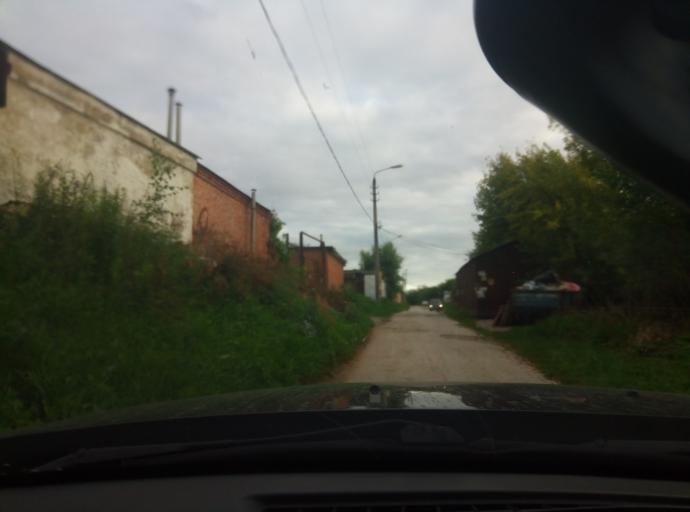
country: RU
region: Tula
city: Mendeleyevskiy
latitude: 54.1673
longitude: 37.5603
